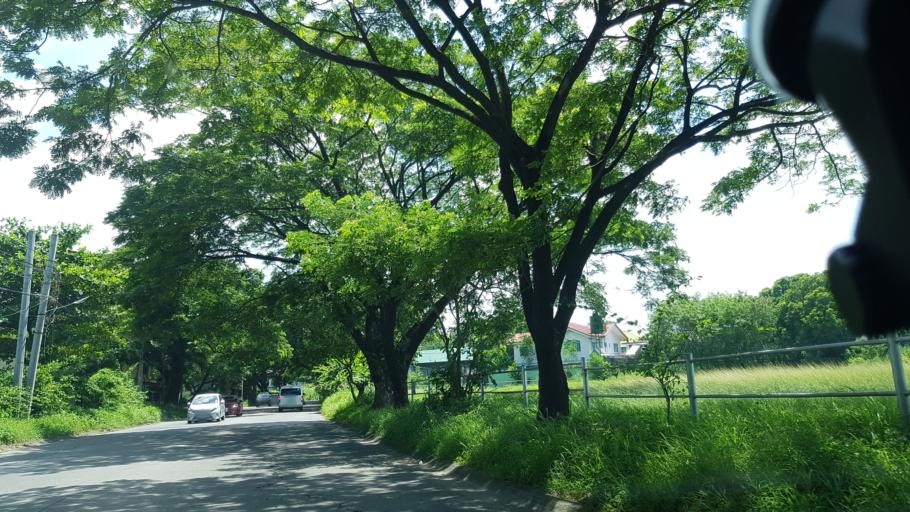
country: PH
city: Sambayanihan People's Village
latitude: 14.4458
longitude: 121.0114
